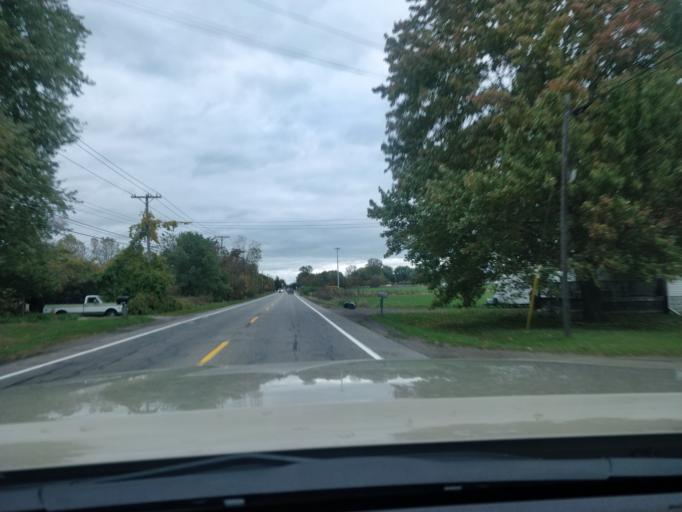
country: US
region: Michigan
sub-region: Wayne County
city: Romulus
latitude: 42.1809
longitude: -83.3309
